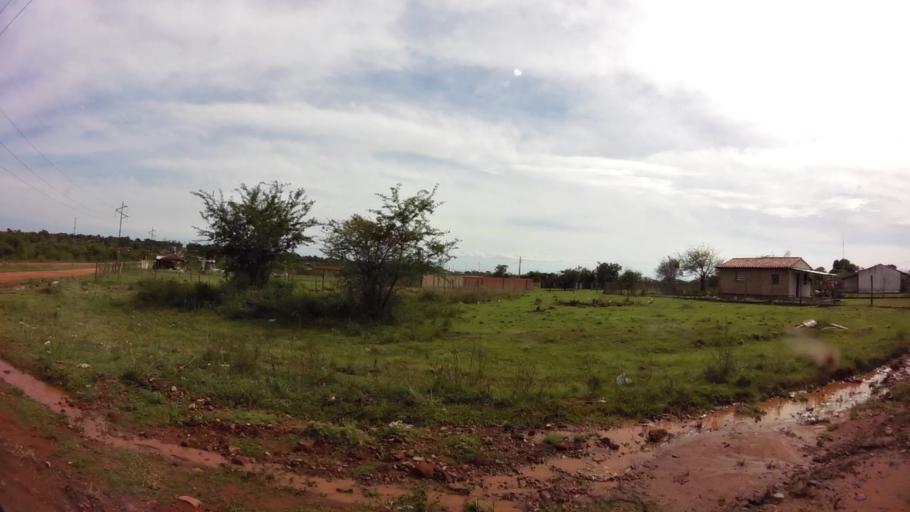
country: PY
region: Central
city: Limpio
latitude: -25.1226
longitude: -57.4813
